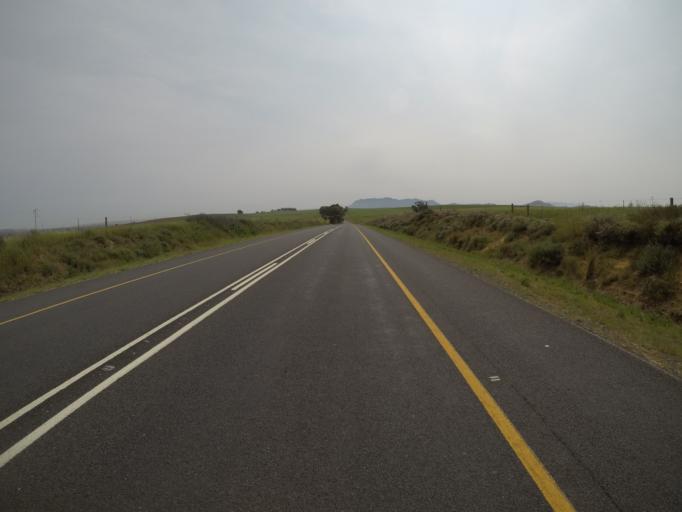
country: ZA
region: Western Cape
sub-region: West Coast District Municipality
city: Malmesbury
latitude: -33.5183
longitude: 18.8463
